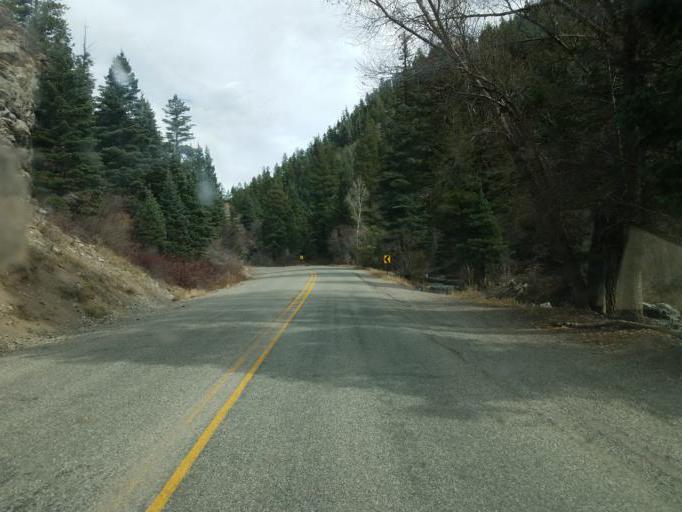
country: US
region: New Mexico
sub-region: Taos County
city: Arroyo Seco
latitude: 36.5659
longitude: -105.5244
